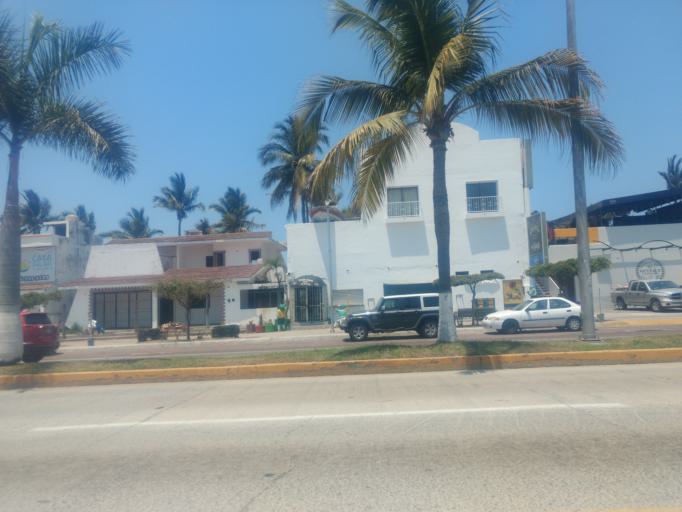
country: MX
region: Colima
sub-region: Manzanillo
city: Manzanillo
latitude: 19.0913
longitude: -104.3147
